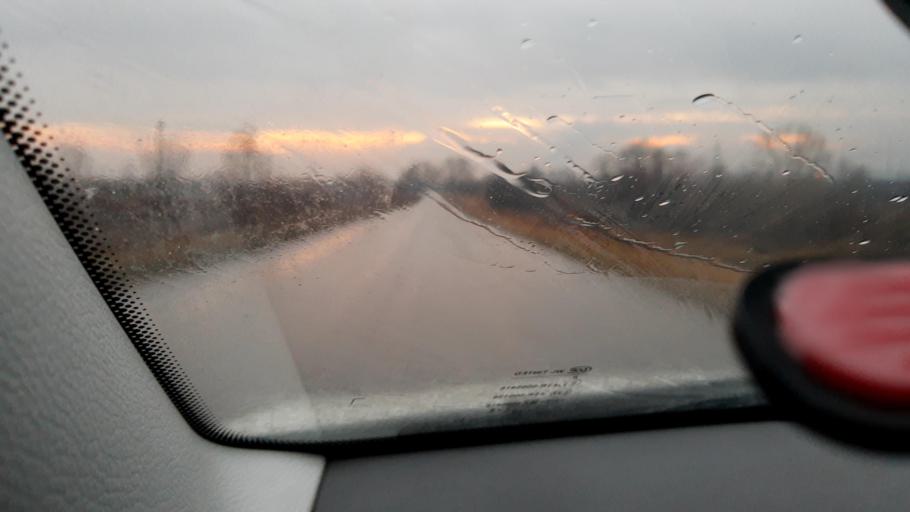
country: RU
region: Bashkortostan
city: Blagoveshchensk
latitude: 54.8869
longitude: 56.1407
